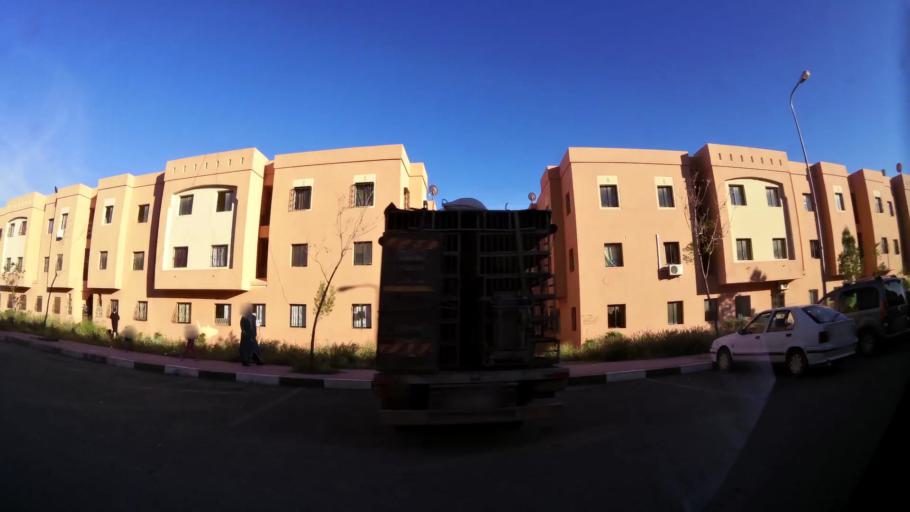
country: MA
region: Marrakech-Tensift-Al Haouz
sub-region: Marrakech
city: Marrakesh
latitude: 31.7635
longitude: -8.1109
